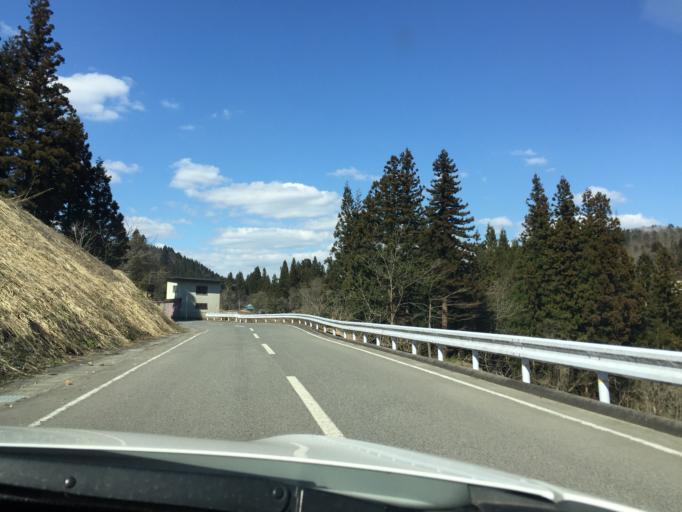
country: JP
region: Yamagata
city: Nagai
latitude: 38.2560
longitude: 140.1036
